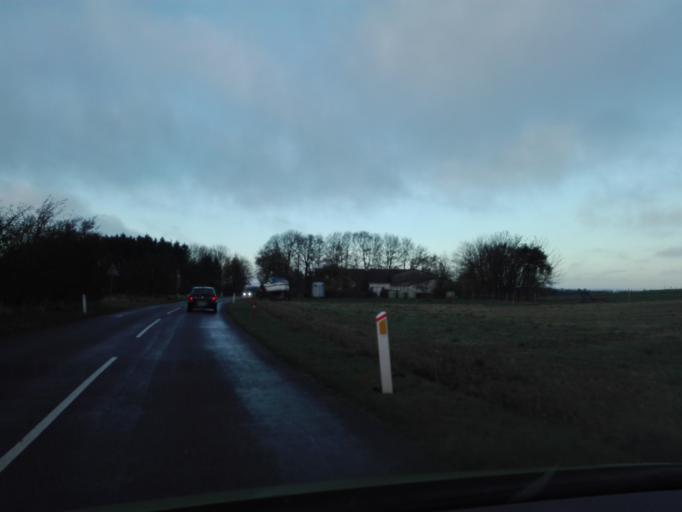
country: DK
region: Central Jutland
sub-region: Skanderborg Kommune
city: Stilling
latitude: 56.0388
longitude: 10.0096
